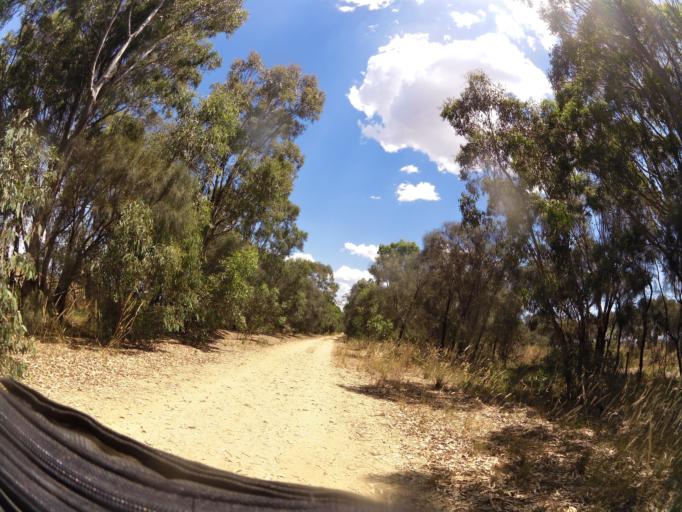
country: AU
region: Victoria
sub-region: Wellington
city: Heyfield
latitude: -37.9810
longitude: 146.8392
